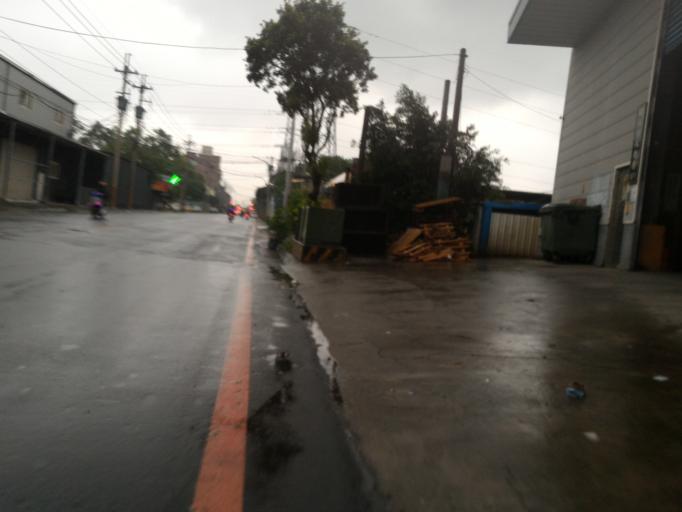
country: TW
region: Taipei
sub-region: Taipei
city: Banqiao
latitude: 24.9723
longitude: 121.4163
